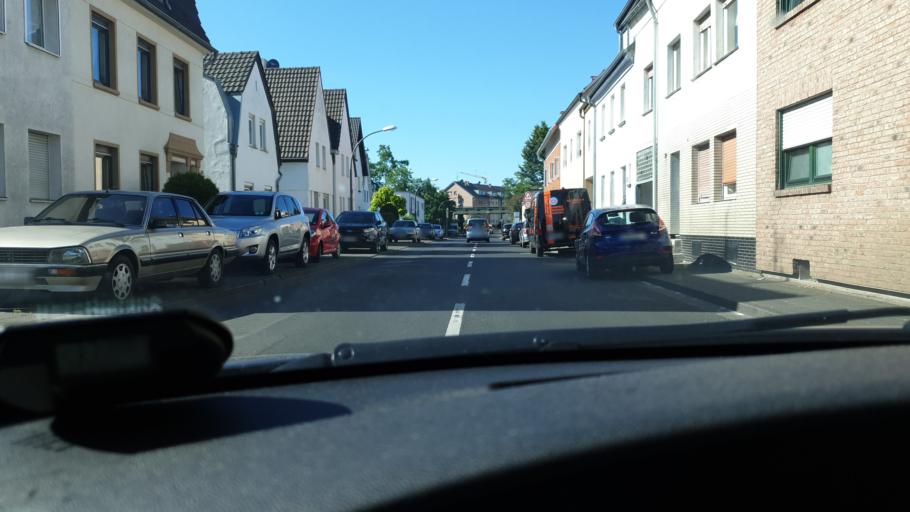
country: DE
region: North Rhine-Westphalia
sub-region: Regierungsbezirk Koln
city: Rath
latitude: 50.9149
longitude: 7.0814
